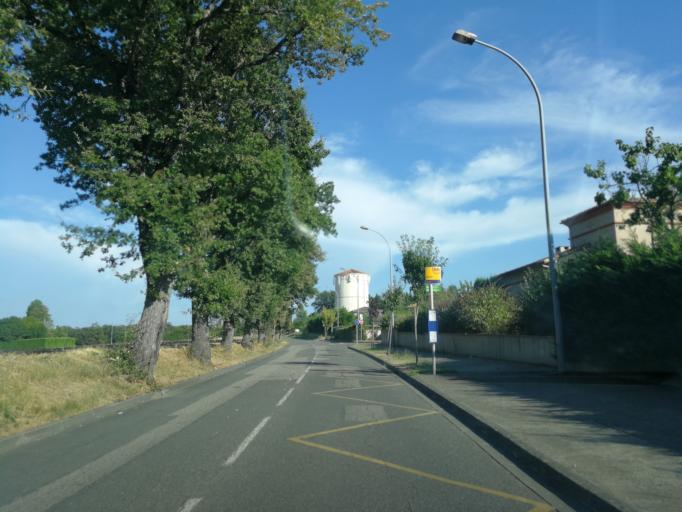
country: FR
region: Midi-Pyrenees
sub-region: Departement de la Haute-Garonne
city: Balma
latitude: 43.6170
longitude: 1.5206
